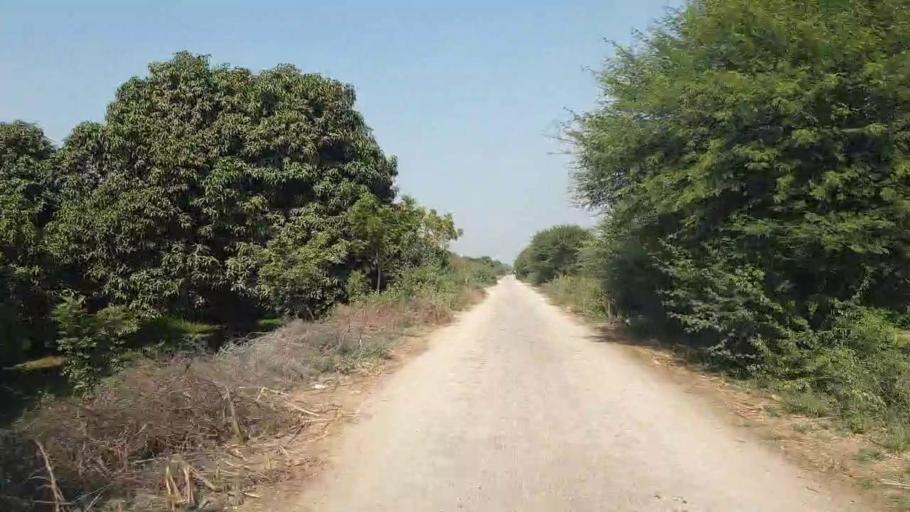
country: PK
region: Sindh
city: Chambar
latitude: 25.4060
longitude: 68.8878
